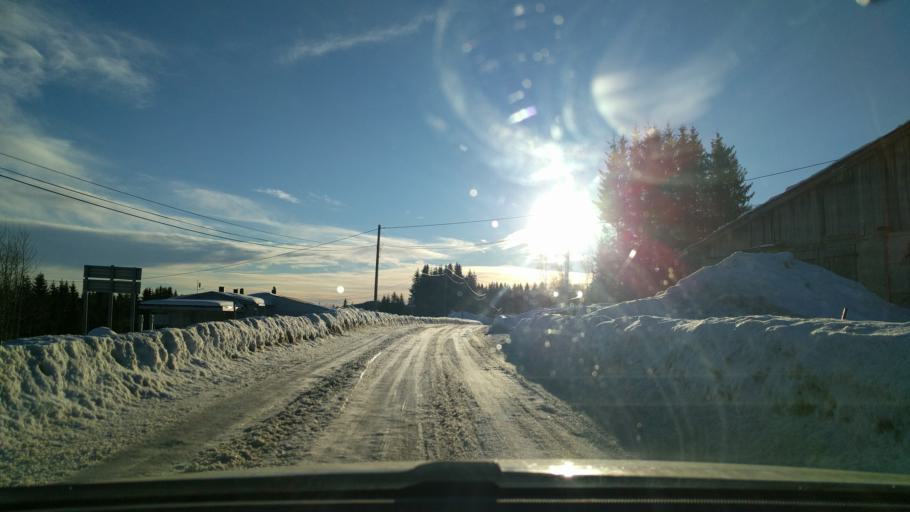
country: NO
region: Hedmark
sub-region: Trysil
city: Innbygda
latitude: 61.1183
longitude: 12.0640
